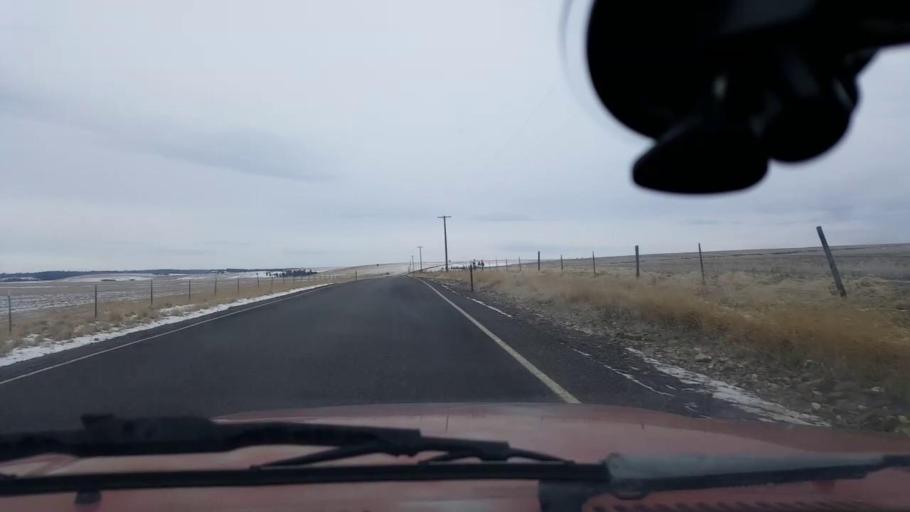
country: US
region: Washington
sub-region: Garfield County
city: Pomeroy
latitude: 46.3213
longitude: -117.3829
